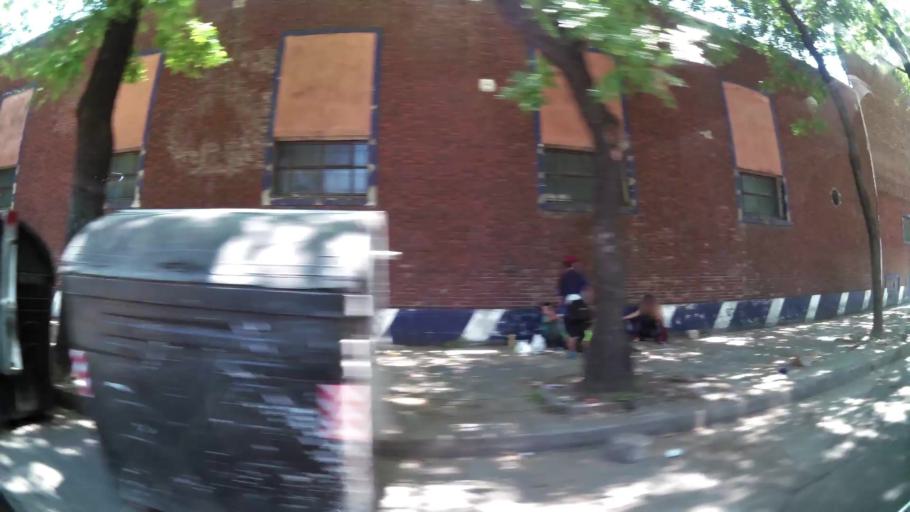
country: AR
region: Buenos Aires
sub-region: Partido de Avellaneda
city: Avellaneda
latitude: -34.6581
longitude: -58.3902
